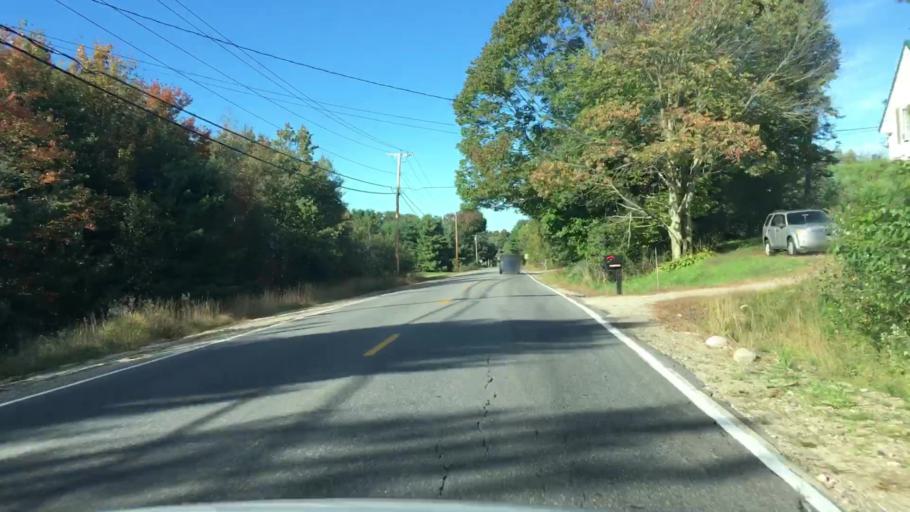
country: US
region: Maine
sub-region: Androscoggin County
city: Lisbon Falls
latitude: 43.9741
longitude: -70.0608
